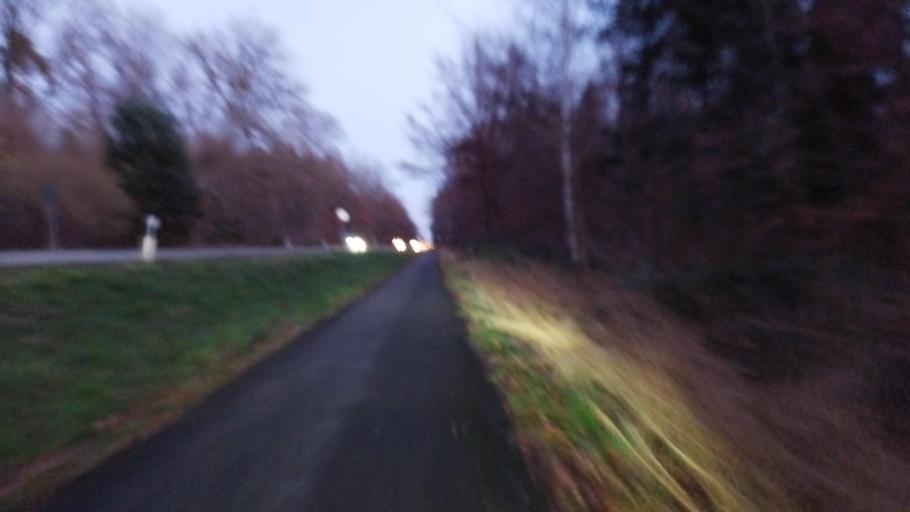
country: DE
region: Rheinland-Pfalz
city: Dudenhofen
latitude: 49.3400
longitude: 8.3982
